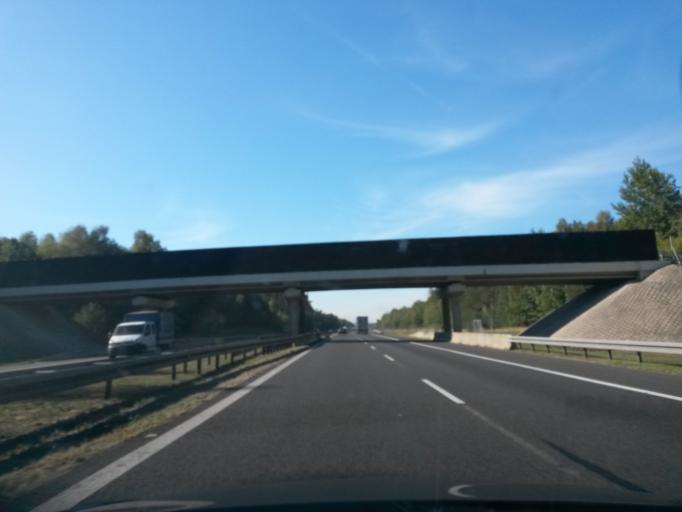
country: PL
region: Opole Voivodeship
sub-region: Powiat opolski
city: Niemodlin
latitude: 50.6711
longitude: 17.6674
